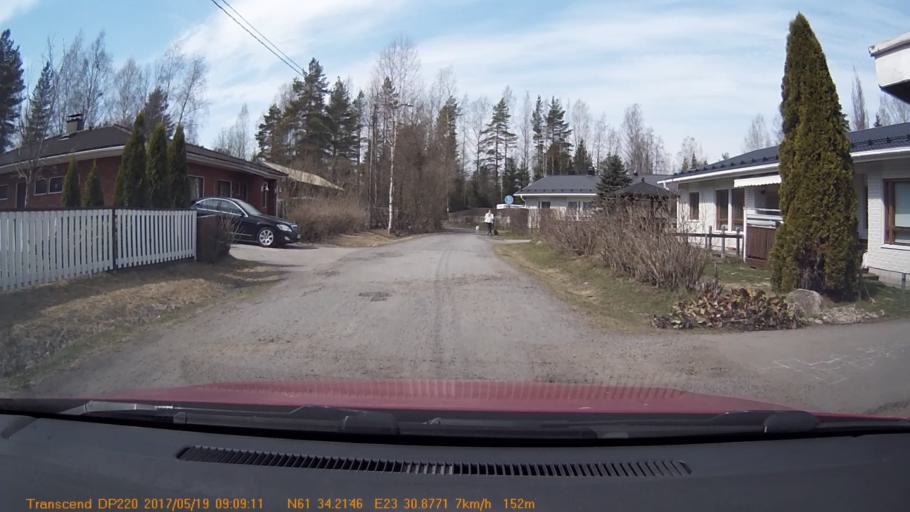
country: FI
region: Pirkanmaa
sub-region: Tampere
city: Yloejaervi
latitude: 61.5702
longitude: 23.5144
